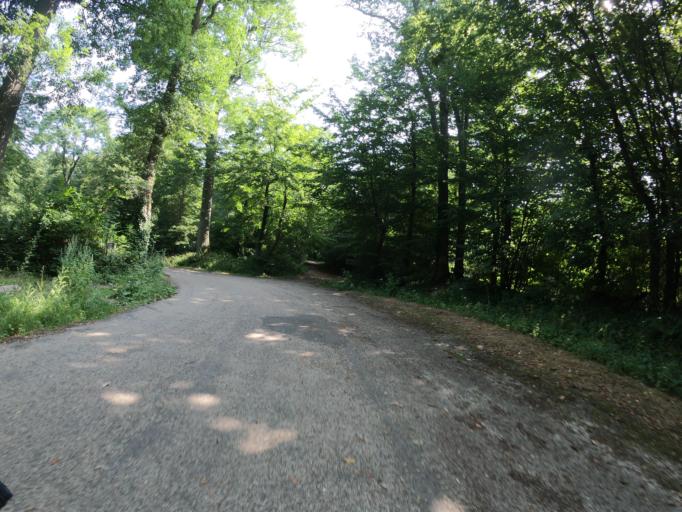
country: FR
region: Ile-de-France
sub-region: Departement de l'Essonne
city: Bievres
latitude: 48.7629
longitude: 2.2363
